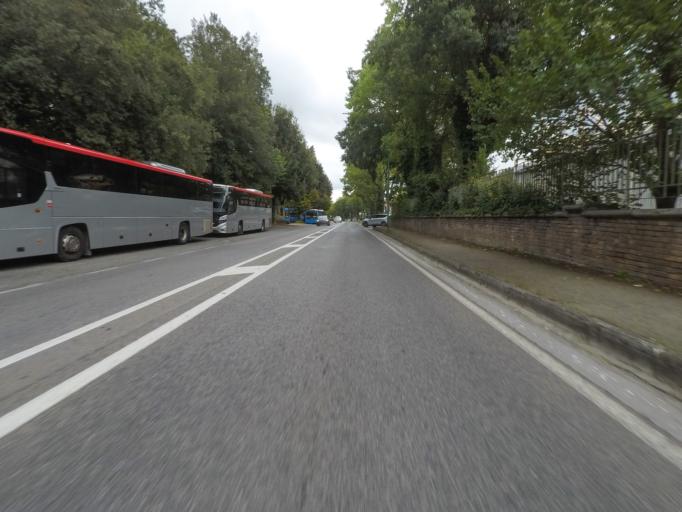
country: IT
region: Tuscany
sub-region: Provincia di Siena
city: Siena
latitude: 43.3250
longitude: 11.3436
